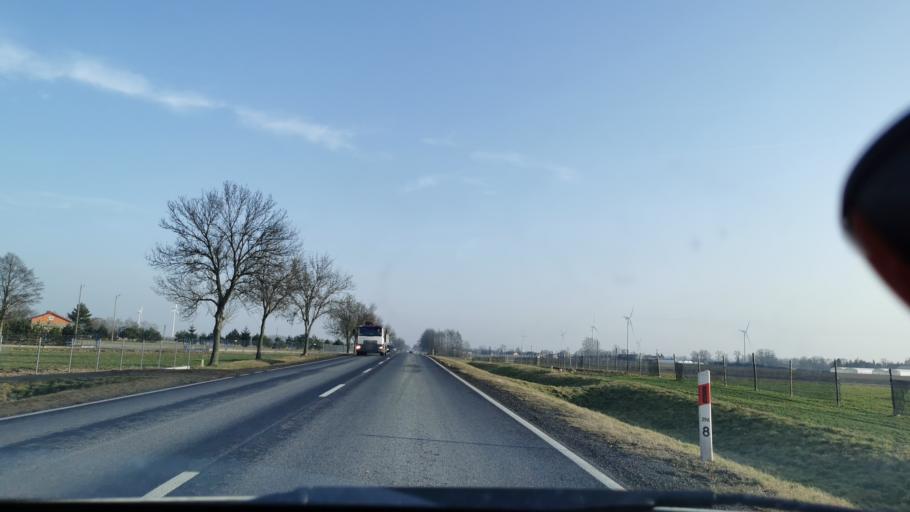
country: PL
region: Lodz Voivodeship
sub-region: Powiat sieradzki
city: Blaszki
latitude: 51.6707
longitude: 18.3727
